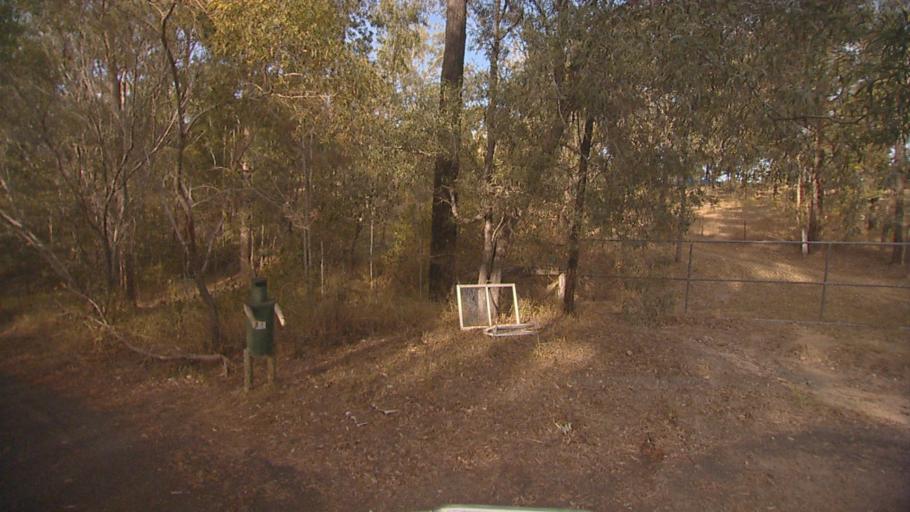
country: AU
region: Queensland
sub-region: Logan
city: Cedar Vale
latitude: -27.8743
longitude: 153.0279
